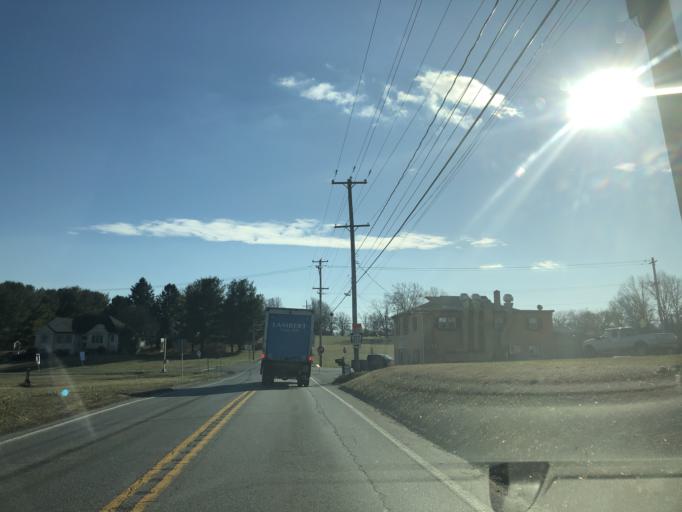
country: US
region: Pennsylvania
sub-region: Chester County
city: South Coatesville
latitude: 39.9555
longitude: -75.8422
